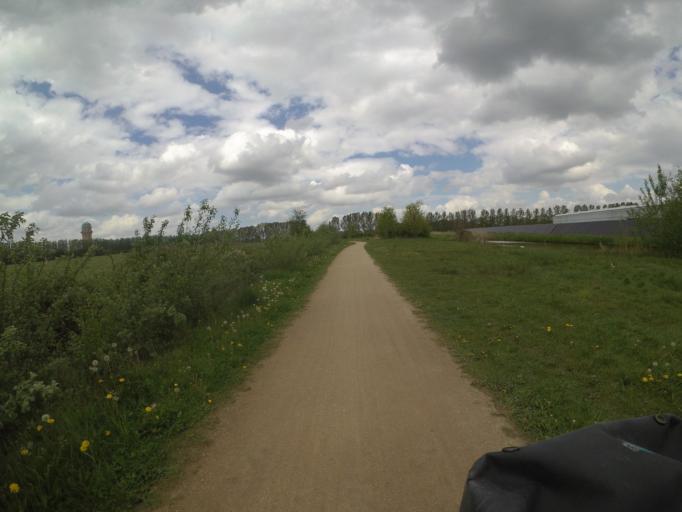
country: NL
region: North Brabant
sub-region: Gemeente Dongen
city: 's Gravenmoer
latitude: 51.6449
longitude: 4.9385
